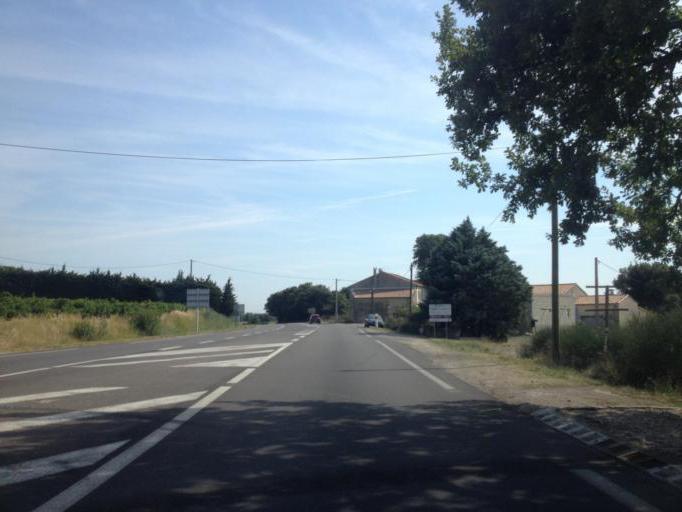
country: FR
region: Provence-Alpes-Cote d'Azur
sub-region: Departement du Vaucluse
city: Vacqueyras
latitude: 44.1498
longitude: 4.9840
